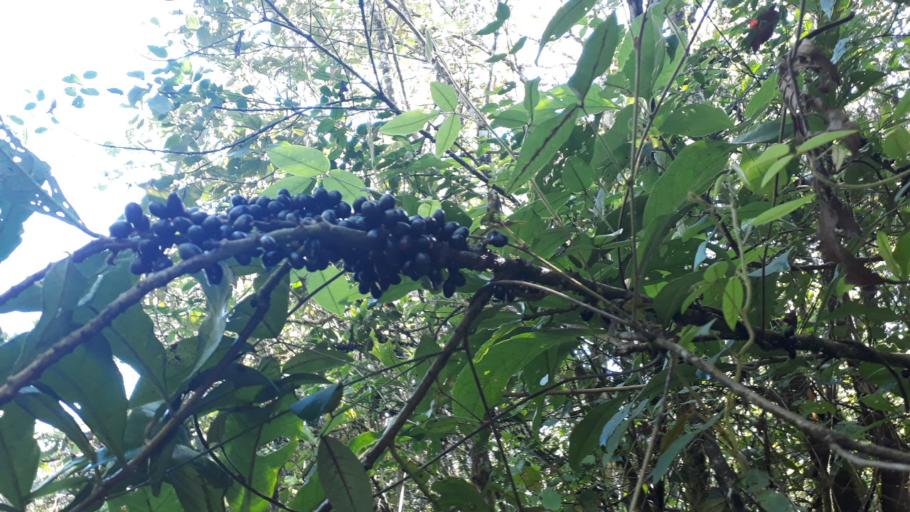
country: CO
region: Casanare
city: Nunchia
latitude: 5.6680
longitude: -72.4236
